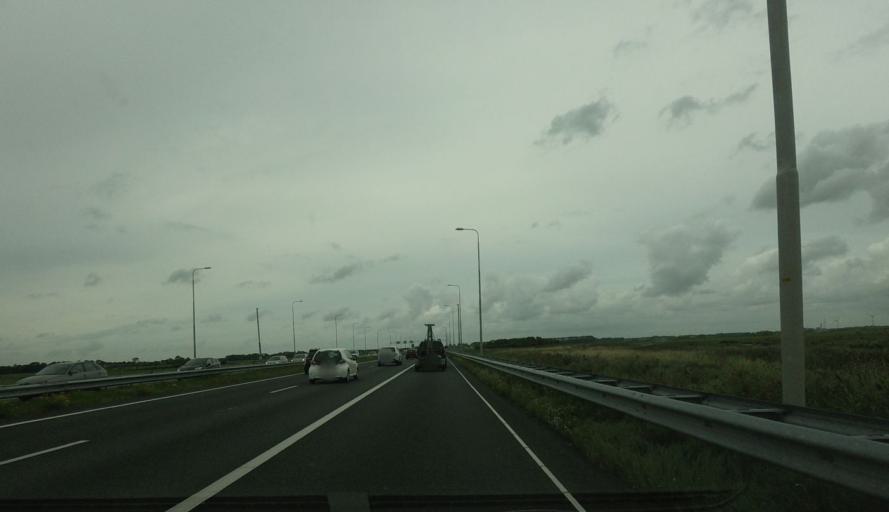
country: NL
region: North Holland
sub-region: Gemeente Uitgeest
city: Uitgeest
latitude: 52.5647
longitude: 4.7171
